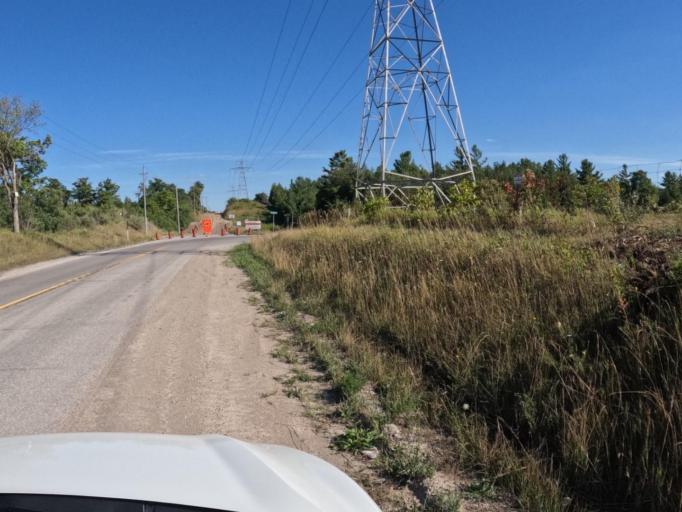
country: CA
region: Ontario
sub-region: Wellington County
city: Guelph
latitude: 43.4452
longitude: -80.1502
